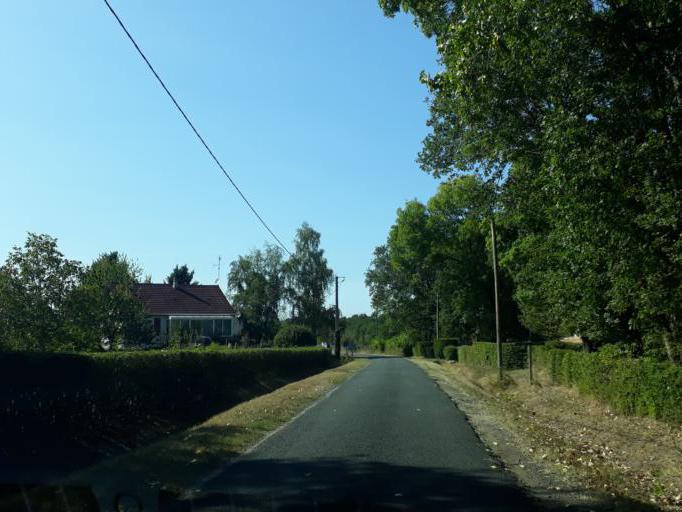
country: FR
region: Centre
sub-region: Departement de l'Indre
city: Chabris
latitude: 47.2586
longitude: 1.6470
